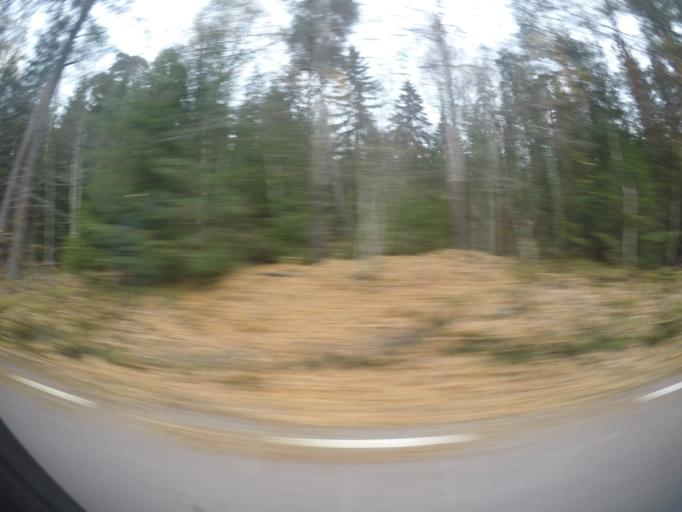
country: SE
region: Vaestmanland
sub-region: Surahammars Kommun
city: Surahammar
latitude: 59.6845
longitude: 16.0857
